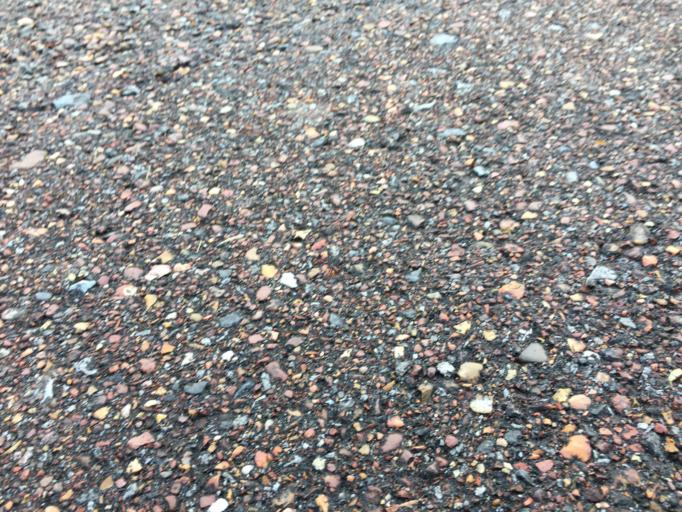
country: US
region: Mississippi
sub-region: De Soto County
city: Olive Branch
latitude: 34.9433
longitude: -89.9238
